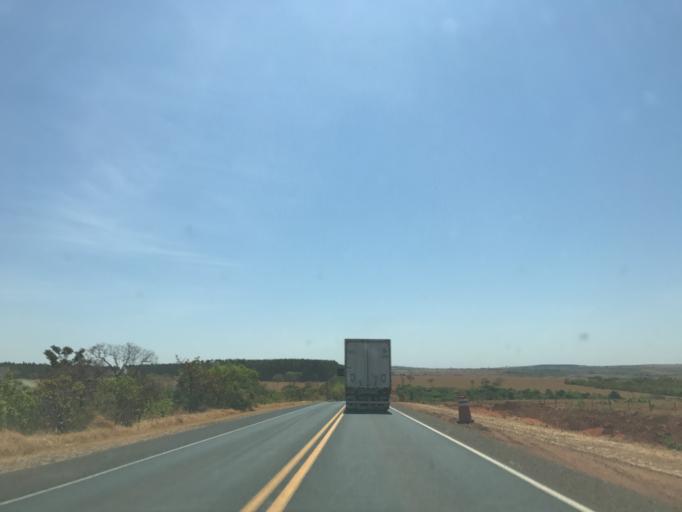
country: BR
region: Minas Gerais
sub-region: Prata
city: Prata
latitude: -19.4583
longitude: -48.8804
